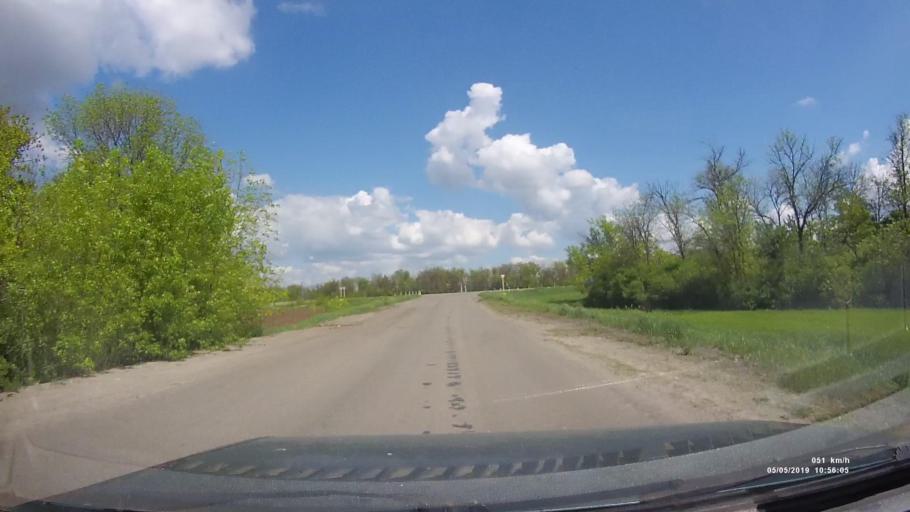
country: RU
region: Rostov
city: Ust'-Donetskiy
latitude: 47.6711
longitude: 40.8202
